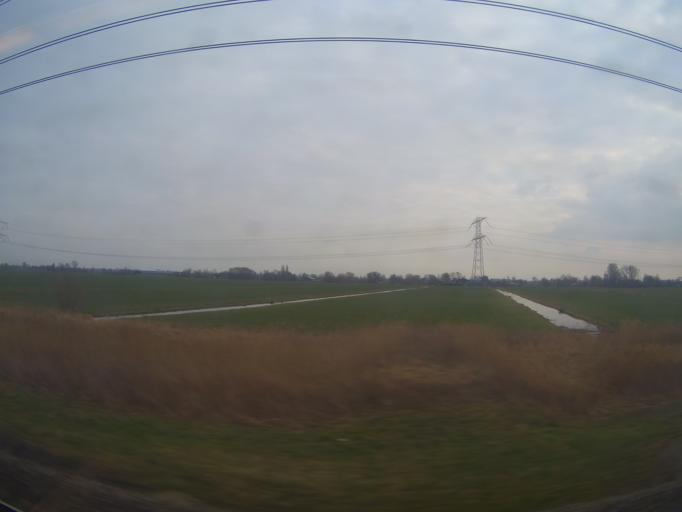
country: NL
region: Utrecht
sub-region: Gemeente Oudewater
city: Oudewater
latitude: 52.0341
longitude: 4.8265
